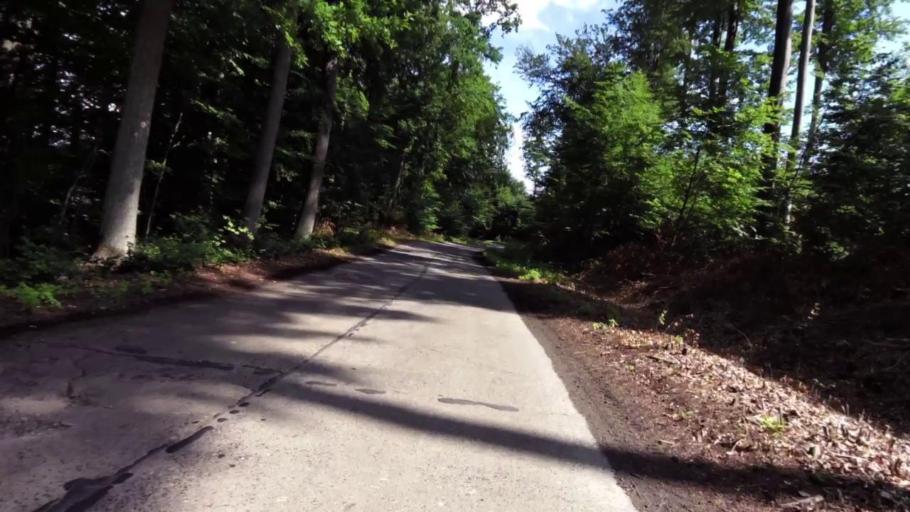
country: PL
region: West Pomeranian Voivodeship
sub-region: Powiat stargardzki
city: Insko
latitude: 53.3912
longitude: 15.5019
